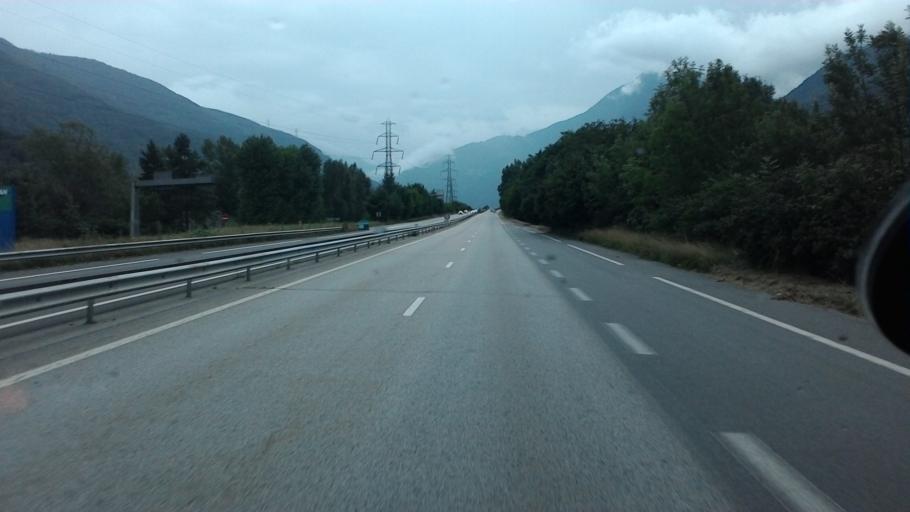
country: FR
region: Rhone-Alpes
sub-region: Departement de la Savoie
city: La Bathie
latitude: 45.6121
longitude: 6.4508
